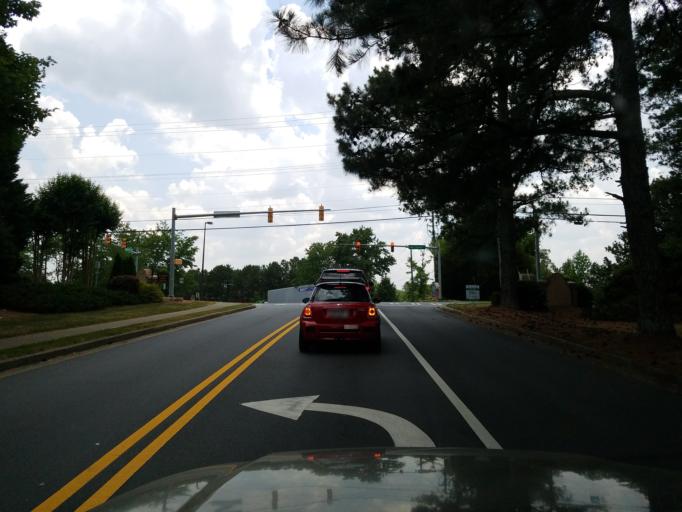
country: US
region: Georgia
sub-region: Fulton County
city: Sandy Springs
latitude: 33.9634
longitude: -84.4255
